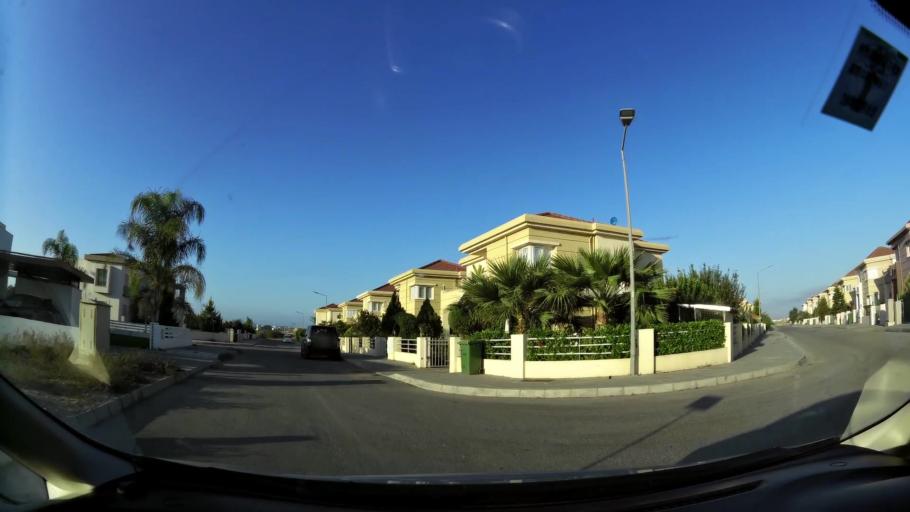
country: CY
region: Lefkosia
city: Nicosia
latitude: 35.1989
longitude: 33.3187
